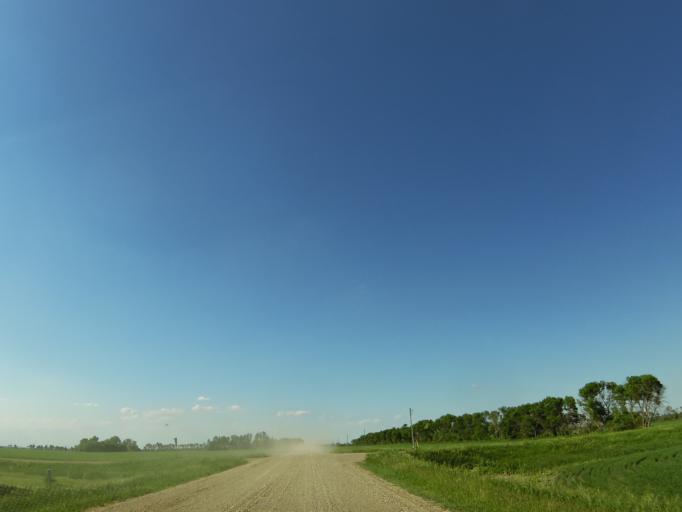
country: US
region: North Dakota
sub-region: Walsh County
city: Grafton
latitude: 48.3532
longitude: -97.2559
